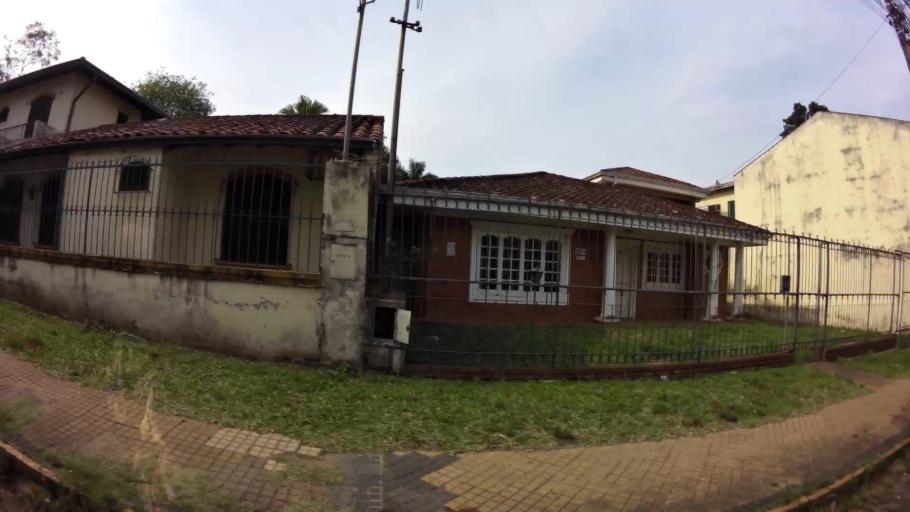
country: PY
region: Central
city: Fernando de la Mora
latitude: -25.2817
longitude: -57.5653
